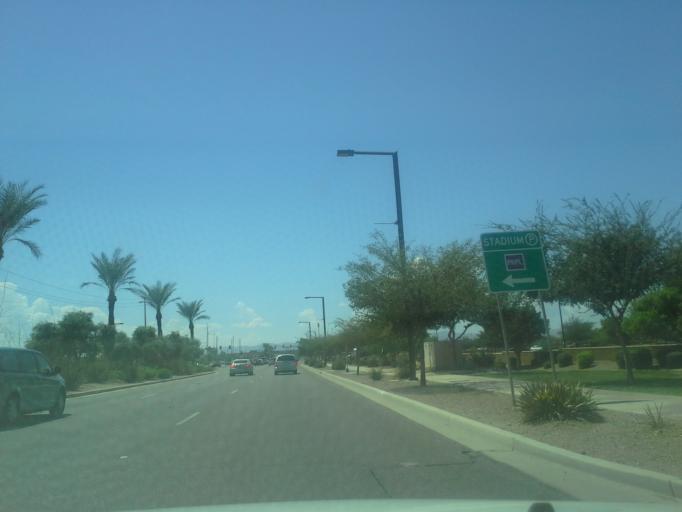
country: US
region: Arizona
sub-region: Maricopa County
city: Peoria
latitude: 33.5375
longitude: -112.2609
